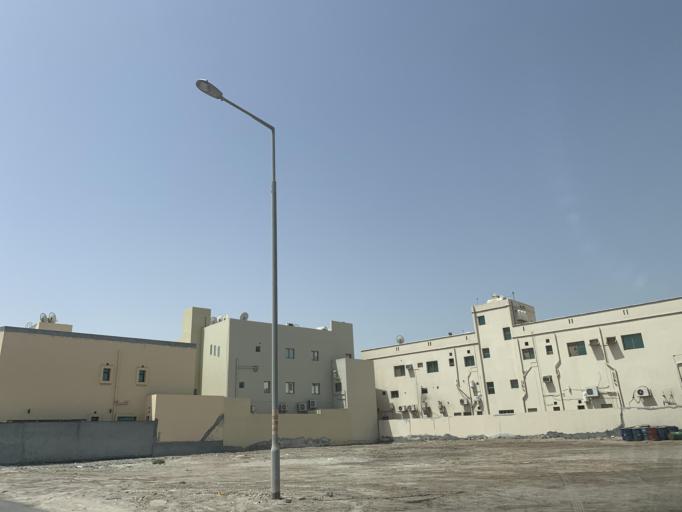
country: BH
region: Northern
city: Sitrah
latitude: 26.1561
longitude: 50.5855
